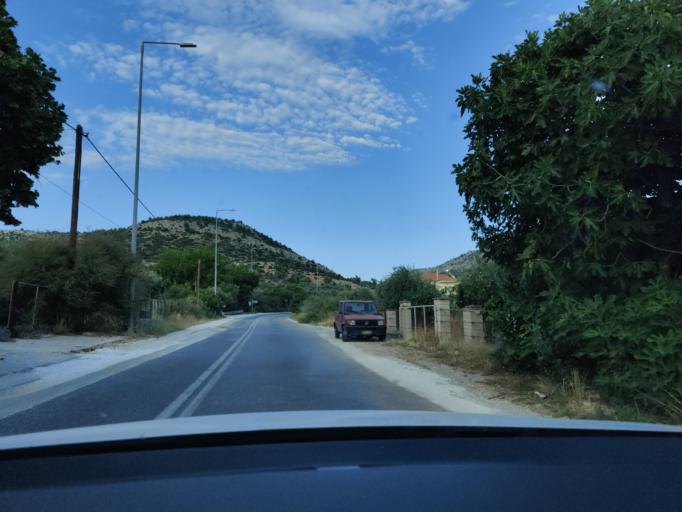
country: GR
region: East Macedonia and Thrace
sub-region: Nomos Kavalas
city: Limenaria
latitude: 40.6134
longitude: 24.6223
